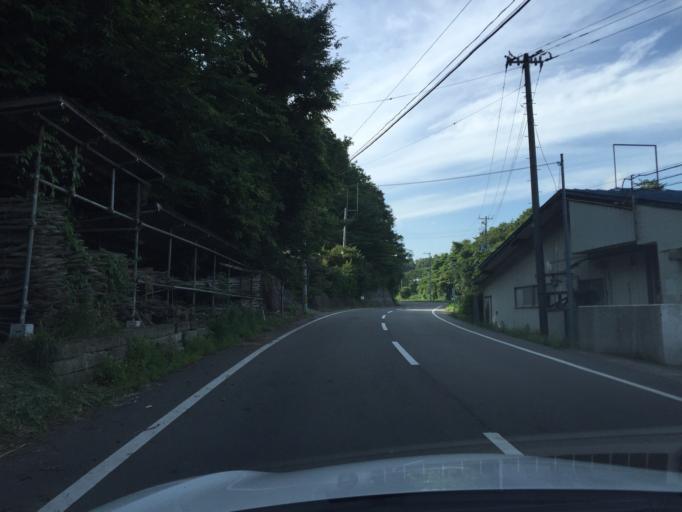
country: JP
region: Fukushima
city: Miharu
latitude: 37.3623
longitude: 140.5186
